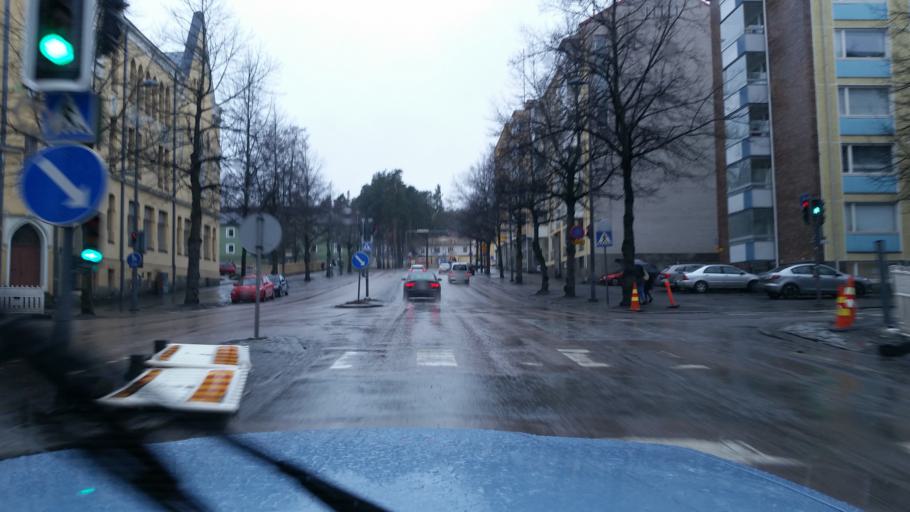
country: FI
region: Pirkanmaa
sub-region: Tampere
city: Tampere
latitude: 61.4944
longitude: 23.7483
